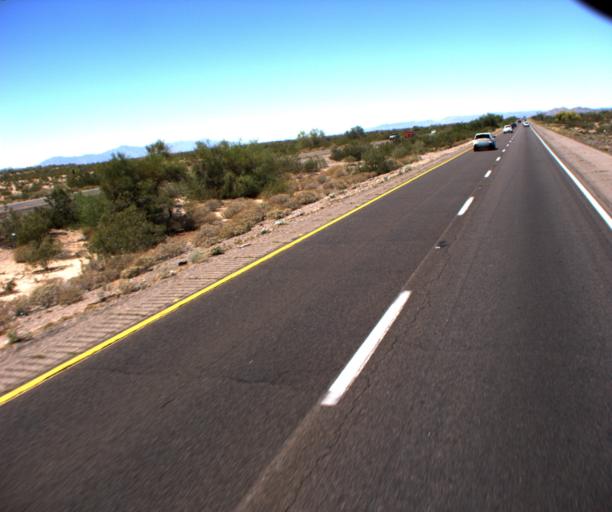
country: US
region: Arizona
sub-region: Pinal County
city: Sacaton
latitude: 33.0570
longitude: -111.7949
